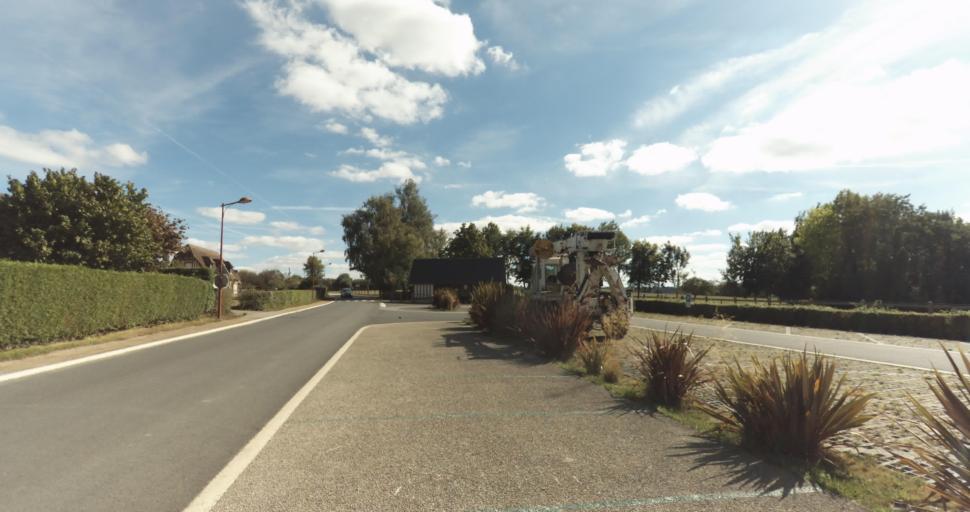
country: FR
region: Lower Normandy
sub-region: Departement de l'Orne
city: Vimoutiers
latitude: 48.9222
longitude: 0.1404
